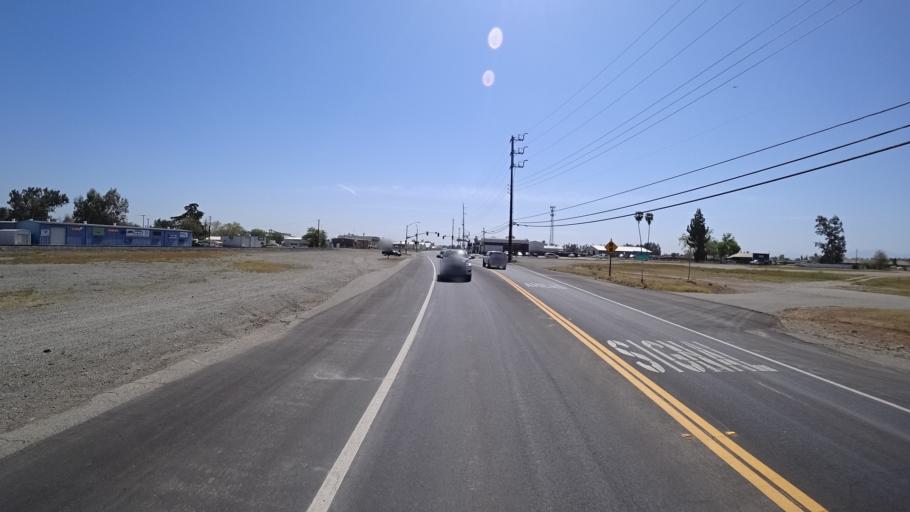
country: US
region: California
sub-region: Glenn County
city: Orland
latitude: 39.7414
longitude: -122.1975
